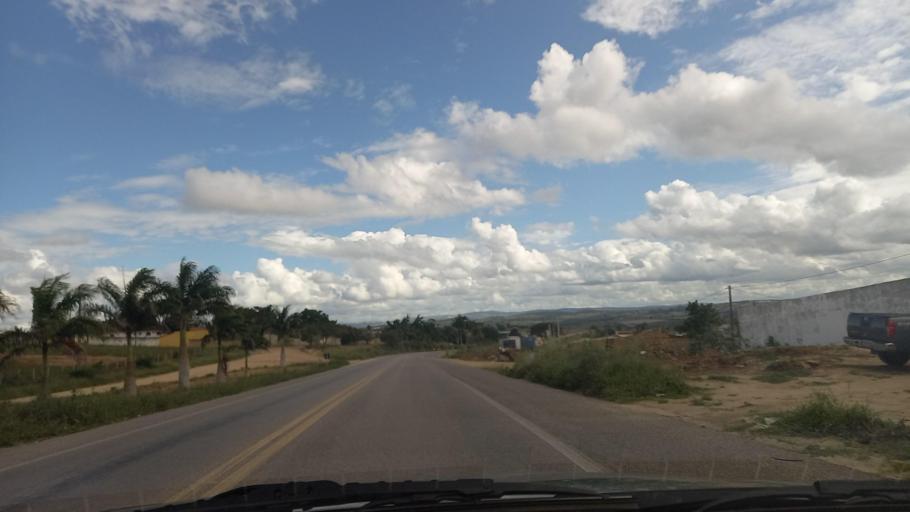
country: BR
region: Pernambuco
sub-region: Lajedo
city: Lajedo
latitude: -8.7157
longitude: -36.4218
